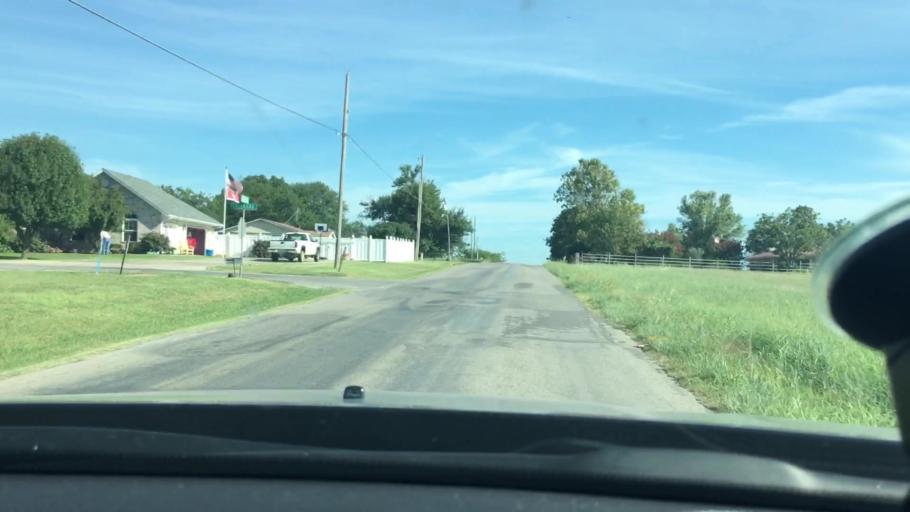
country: US
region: Oklahoma
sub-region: Carter County
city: Lone Grove
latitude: 34.1845
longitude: -97.2475
